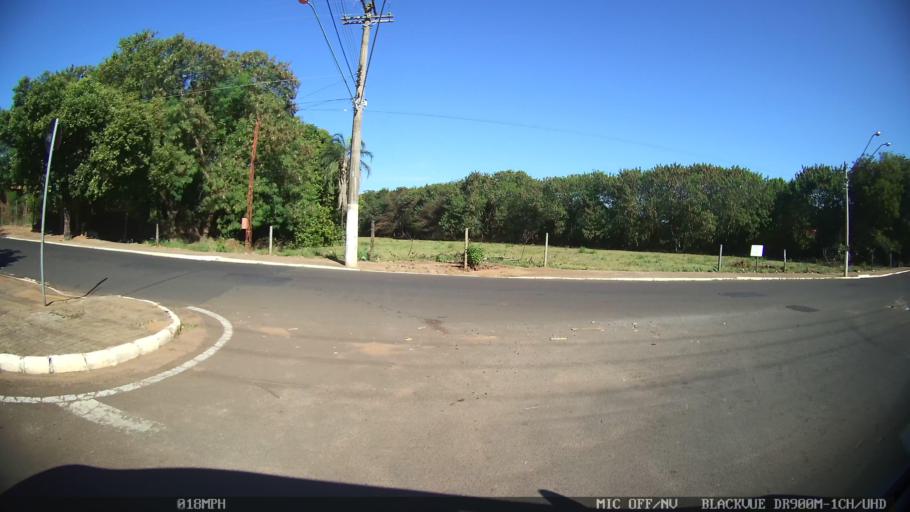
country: BR
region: Sao Paulo
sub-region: Olimpia
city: Olimpia
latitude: -20.7438
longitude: -48.9048
